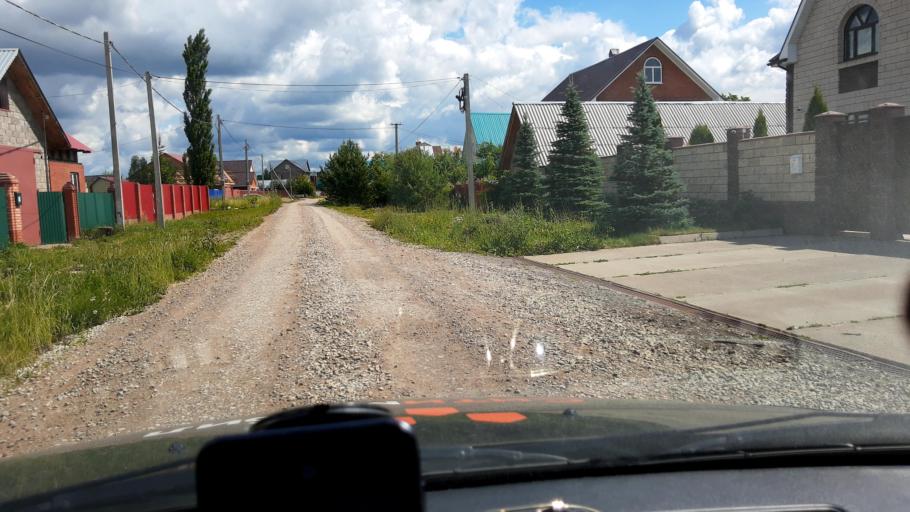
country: RU
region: Bashkortostan
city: Iglino
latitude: 54.7892
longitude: 56.2472
